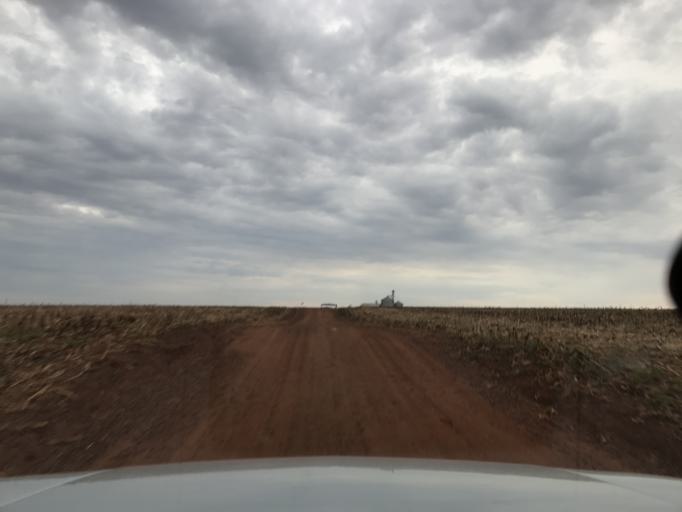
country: BR
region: Parana
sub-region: Palotina
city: Palotina
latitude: -24.2235
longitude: -53.8378
